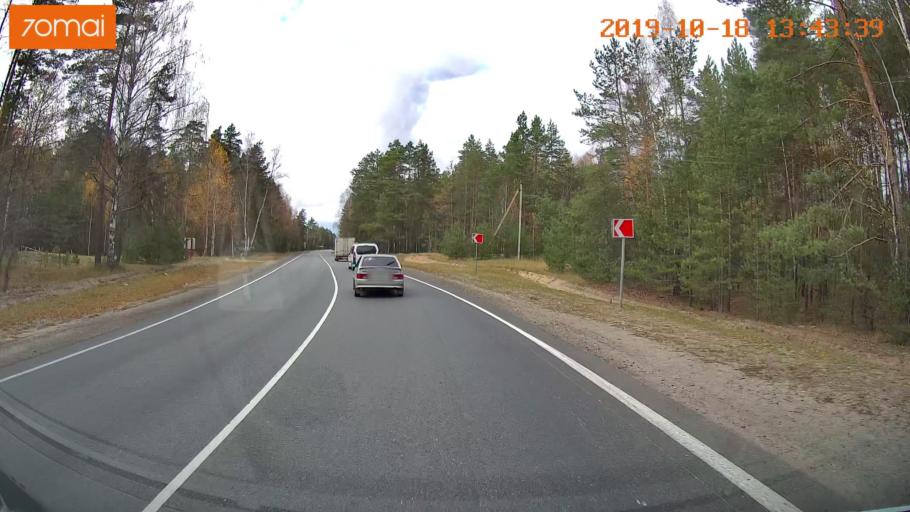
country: RU
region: Rjazan
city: Solotcha
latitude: 54.9319
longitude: 39.9738
